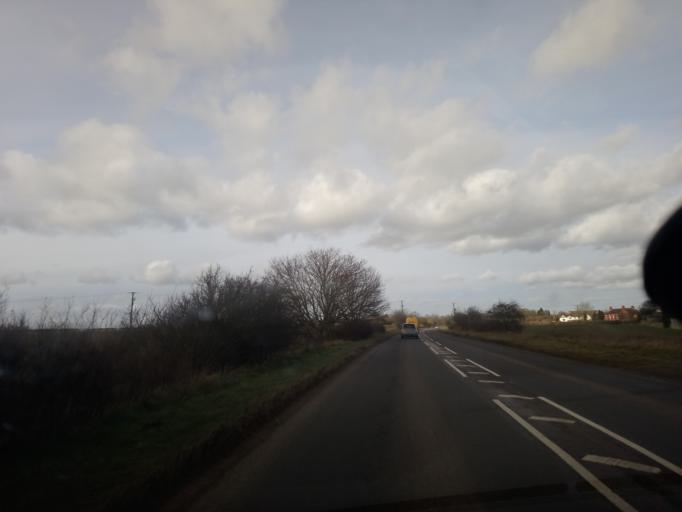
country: GB
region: England
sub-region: Telford and Wrekin
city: Eyton upon the Weald Moors
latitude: 52.7758
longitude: -2.5528
